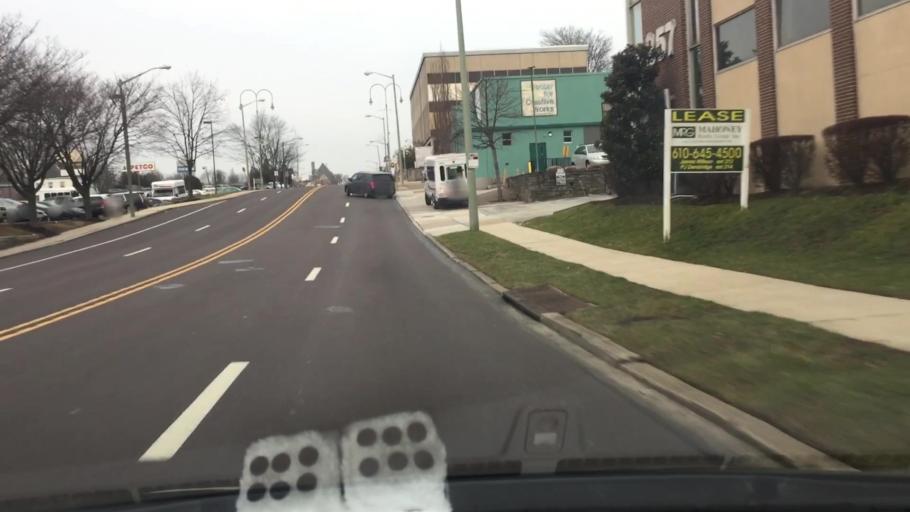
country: US
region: Pennsylvania
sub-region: Montgomery County
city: Ardmore
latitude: 40.0035
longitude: -75.2820
